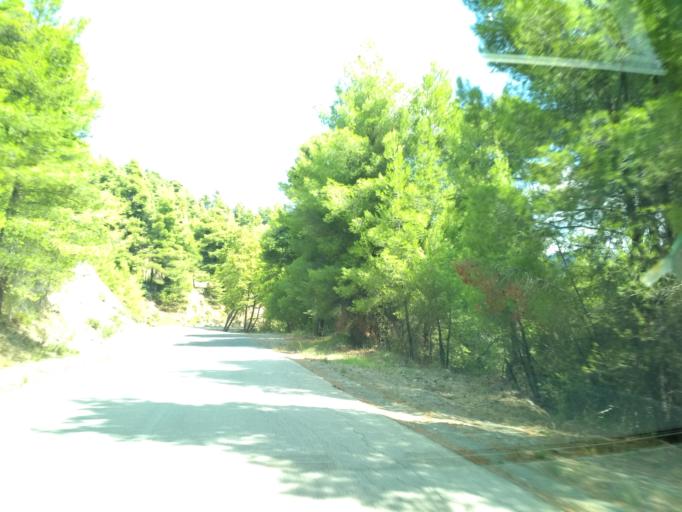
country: GR
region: Central Greece
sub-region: Nomos Evvoias
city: Roviai
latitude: 38.8323
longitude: 23.2843
